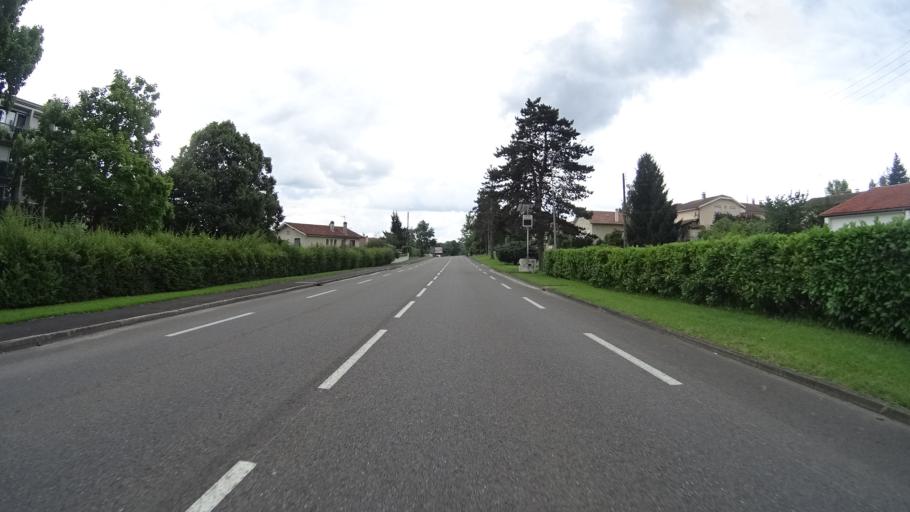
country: FR
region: Aquitaine
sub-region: Departement des Pyrenees-Atlantiques
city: Orthez
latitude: 43.4951
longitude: -0.7796
